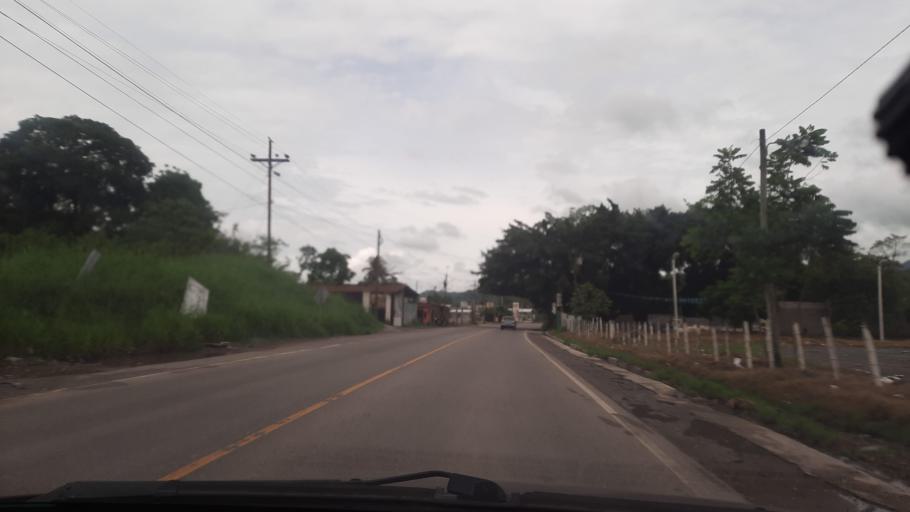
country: GT
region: Izabal
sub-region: Municipio de Los Amates
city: Los Amates
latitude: 15.2536
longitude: -89.1030
